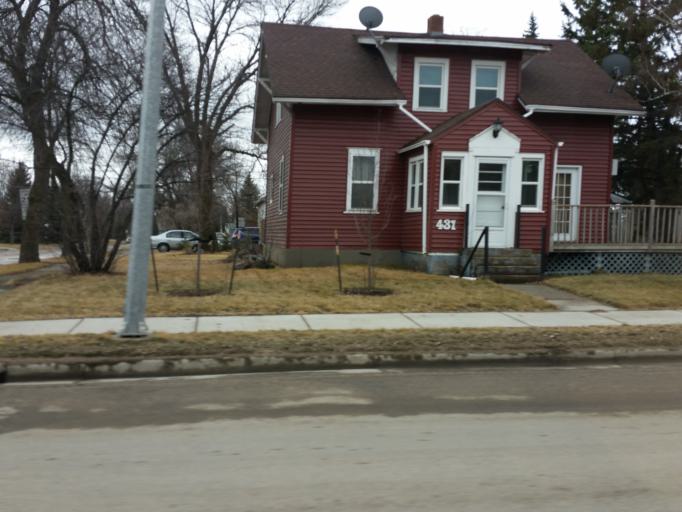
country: US
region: North Dakota
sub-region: Traill County
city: Mayville
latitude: 47.4980
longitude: -97.3197
